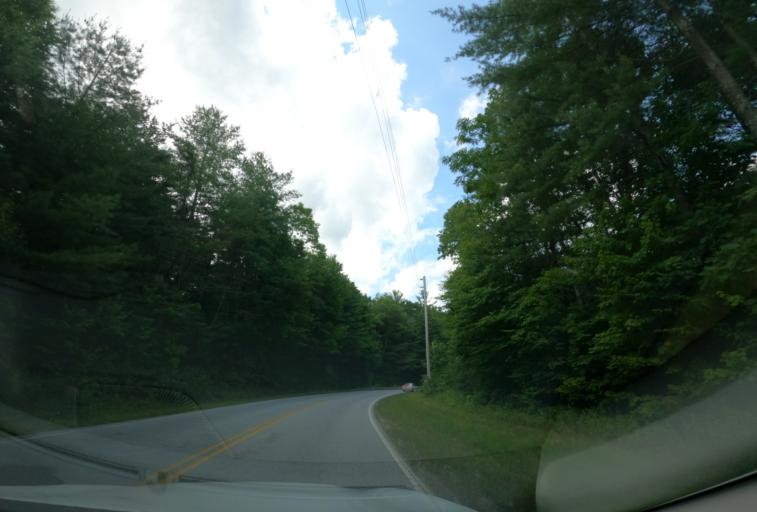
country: US
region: North Carolina
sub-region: Transylvania County
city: Brevard
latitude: 35.0996
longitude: -82.9669
